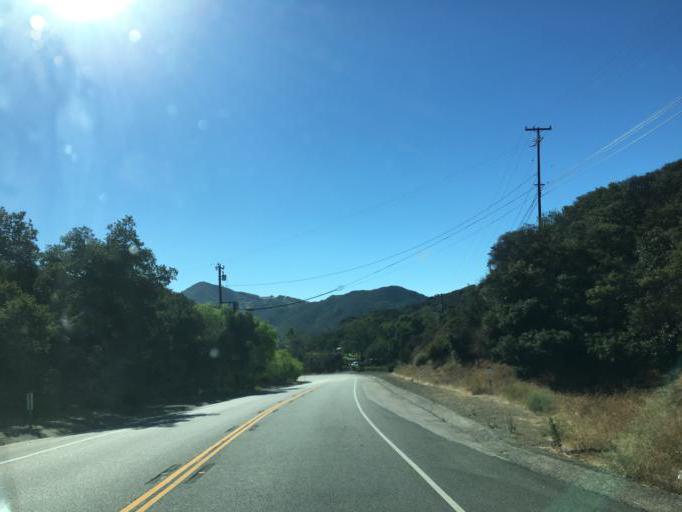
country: US
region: California
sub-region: Los Angeles County
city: Westlake Village
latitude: 34.0947
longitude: -118.8255
